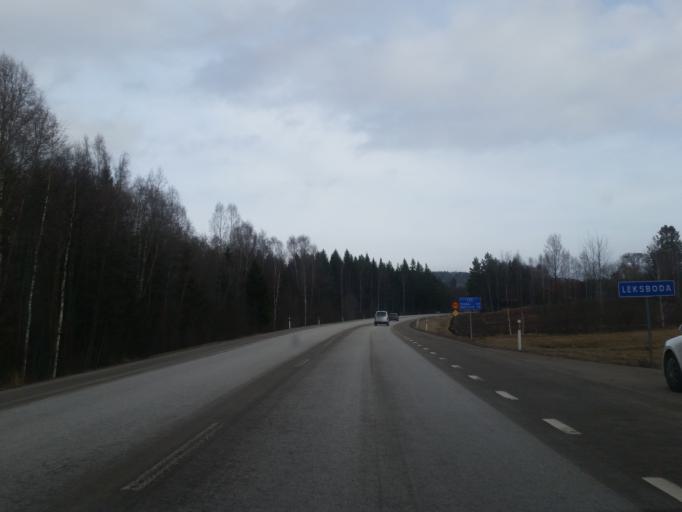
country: SE
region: Dalarna
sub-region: Leksand Municipality
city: Leksand
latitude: 60.7808
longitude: 15.0240
